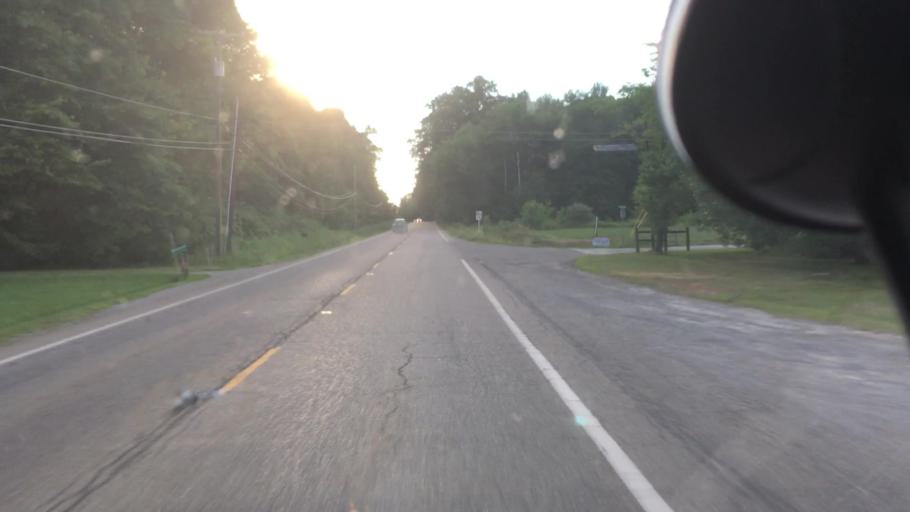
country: US
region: Ohio
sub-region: Columbiana County
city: New Waterford
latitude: 40.8770
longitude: -80.5940
